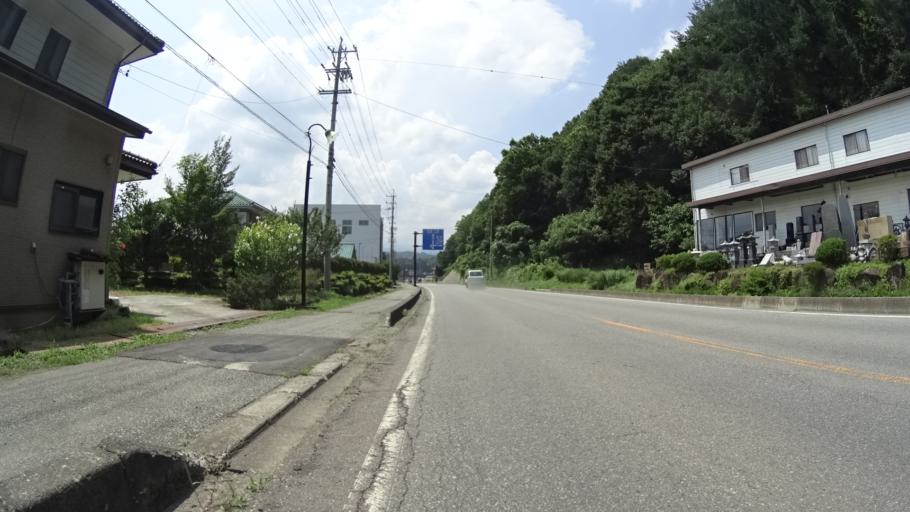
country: JP
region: Nagano
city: Saku
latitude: 36.1552
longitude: 138.4963
